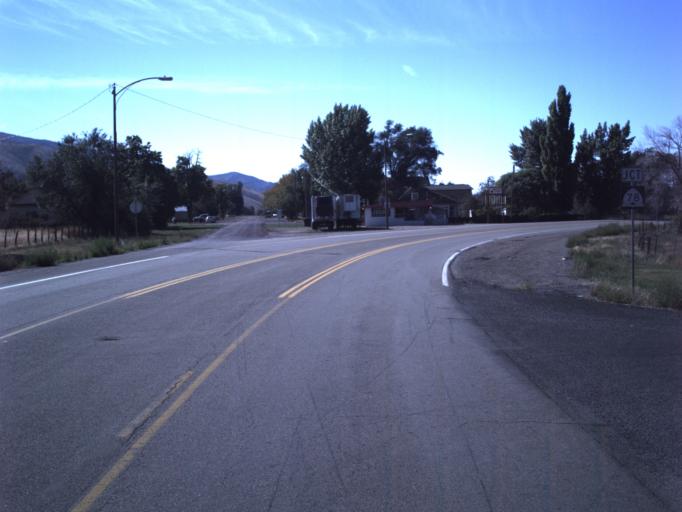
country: US
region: Utah
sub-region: Juab County
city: Nephi
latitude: 39.5605
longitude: -111.8620
